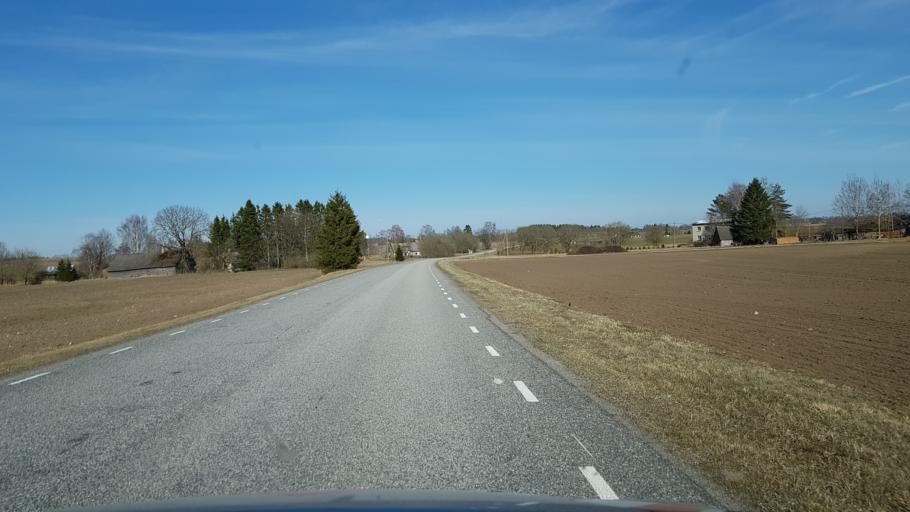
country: EE
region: Laeaene-Virumaa
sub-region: Vinni vald
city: Vinni
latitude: 59.0651
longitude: 26.4798
